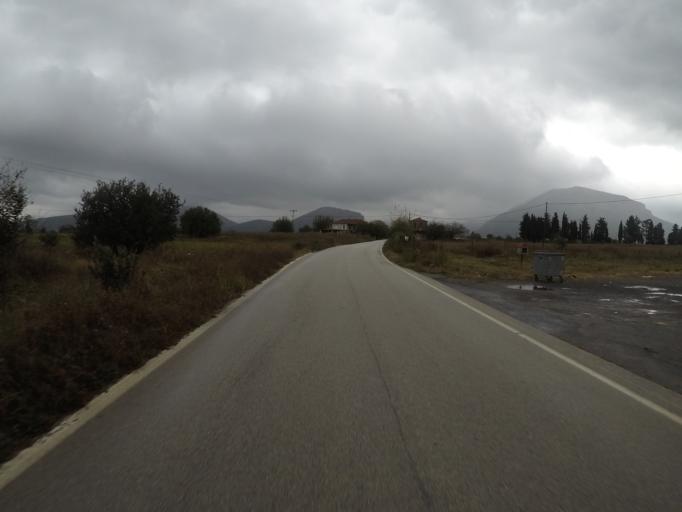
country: GR
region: Peloponnese
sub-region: Nomos Arkadias
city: Tripoli
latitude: 37.5770
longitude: 22.4142
